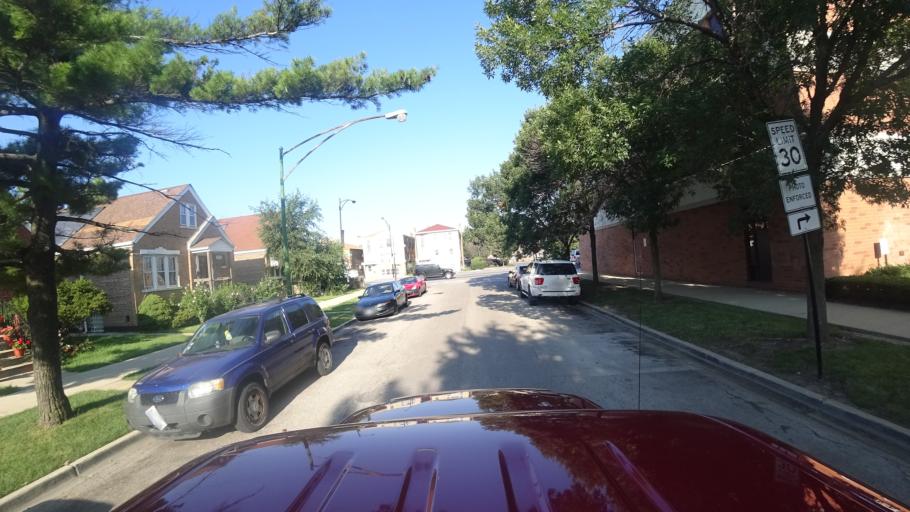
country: US
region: Illinois
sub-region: Cook County
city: Hometown
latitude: 41.7923
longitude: -87.7226
